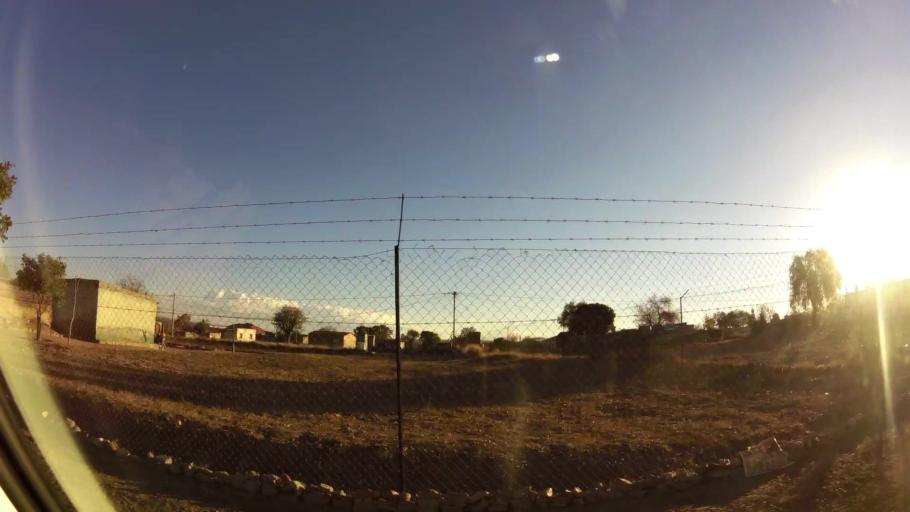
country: ZA
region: Limpopo
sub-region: Capricorn District Municipality
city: Polokwane
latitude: -23.8230
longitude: 29.3782
